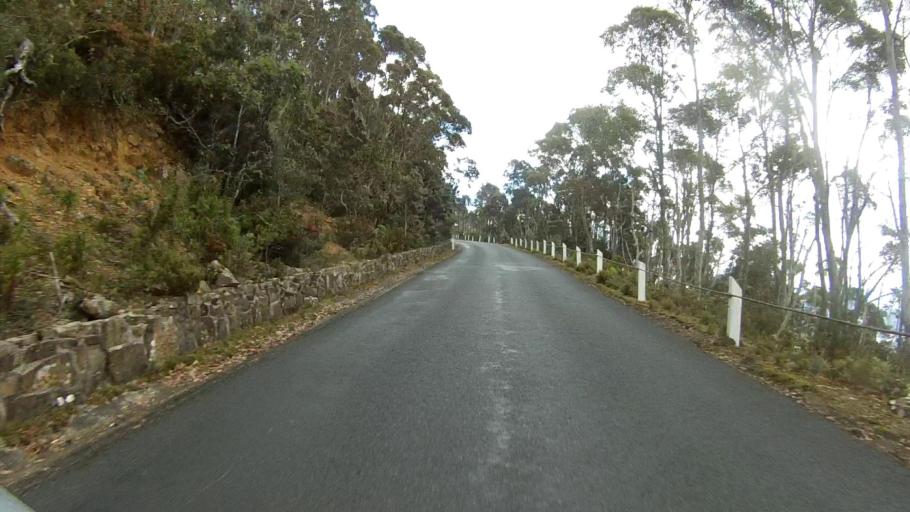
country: AU
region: Tasmania
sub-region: Glenorchy
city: West Moonah
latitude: -42.8957
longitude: 147.2446
